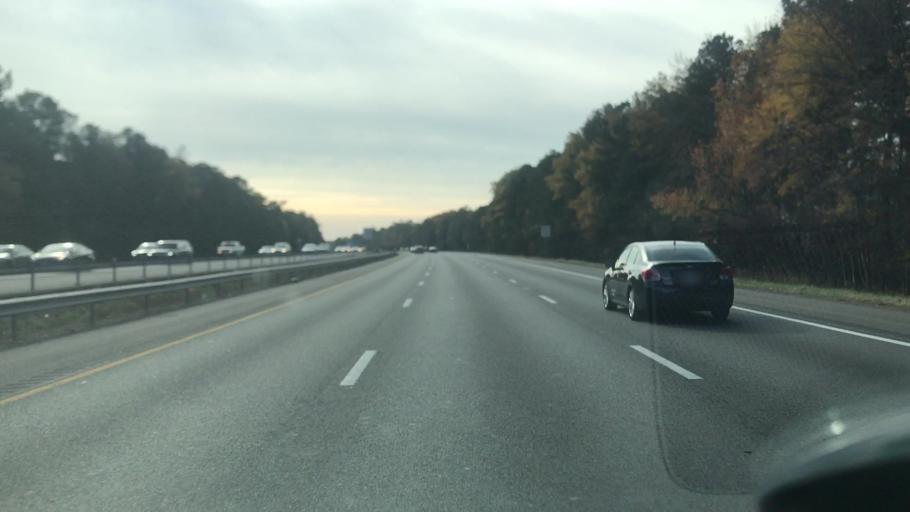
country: US
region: Virginia
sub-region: Hanover County
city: Ashland
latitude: 37.7721
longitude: -77.4624
